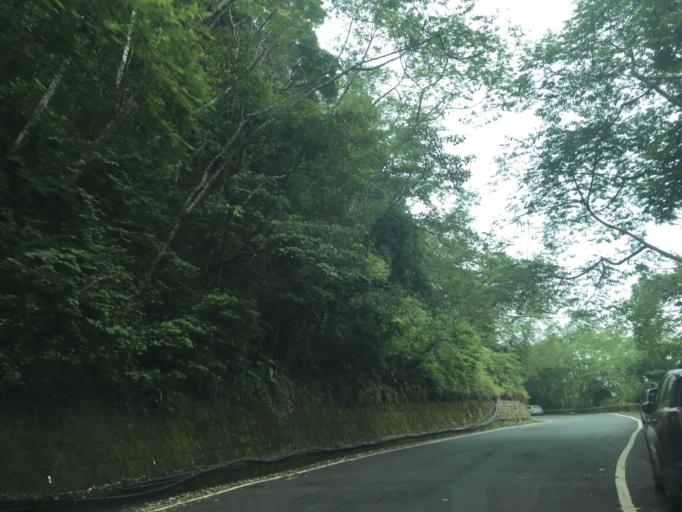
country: TW
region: Taiwan
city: Fengyuan
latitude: 24.2498
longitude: 120.9181
